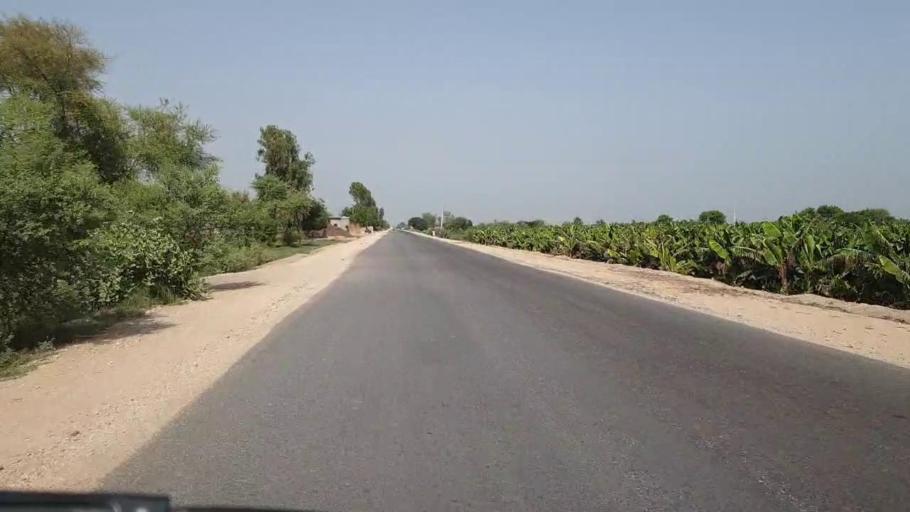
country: PK
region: Sindh
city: Sakrand
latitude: 26.2451
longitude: 68.2444
